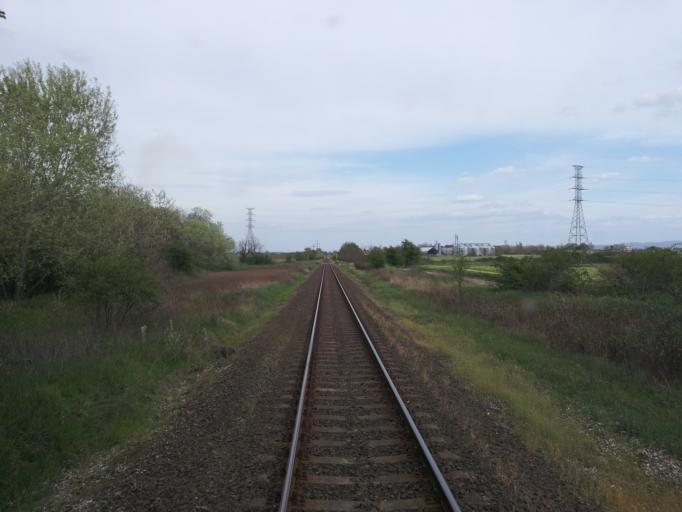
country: HU
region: Komarom-Esztergom
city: Komarom
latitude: 47.6986
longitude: 18.0907
